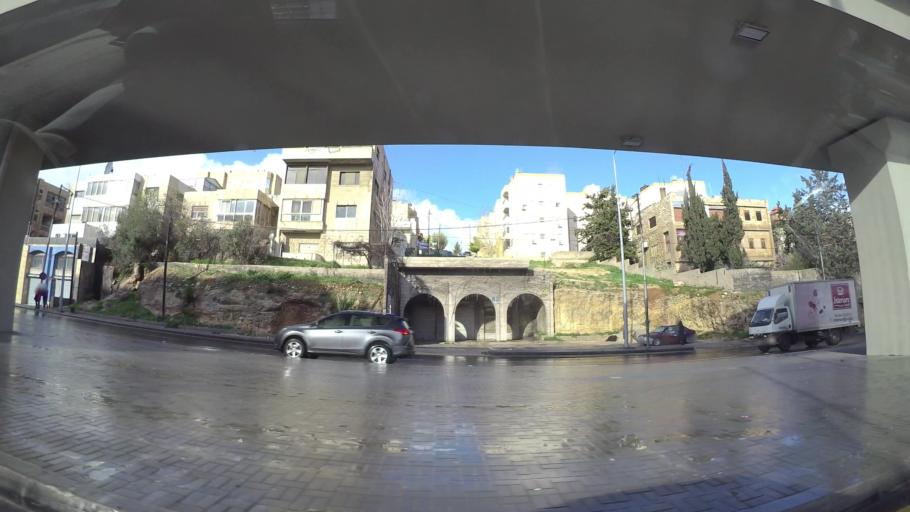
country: JO
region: Amman
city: Al Jubayhah
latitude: 31.9938
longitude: 35.8880
